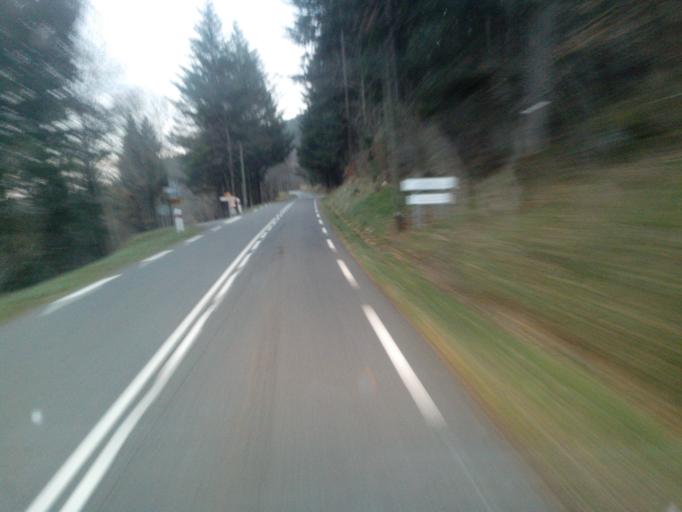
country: FR
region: Languedoc-Roussillon
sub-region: Departement du Gard
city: Valleraugue
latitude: 44.1858
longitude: 3.6721
